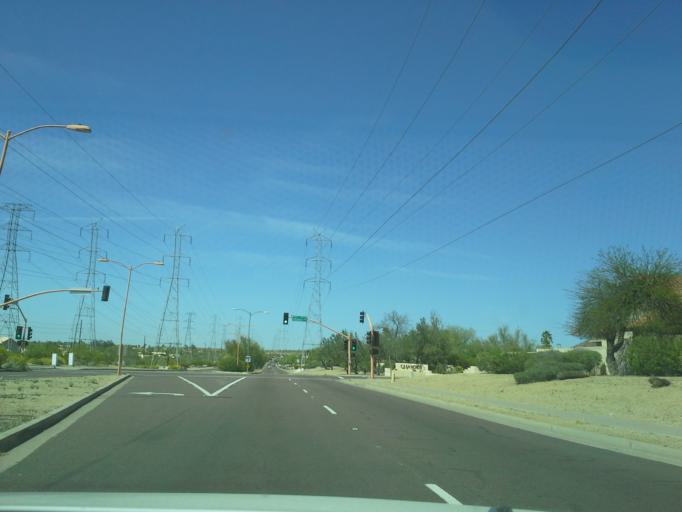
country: US
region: Arizona
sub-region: Maricopa County
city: Scottsdale
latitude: 33.5913
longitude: -111.8380
